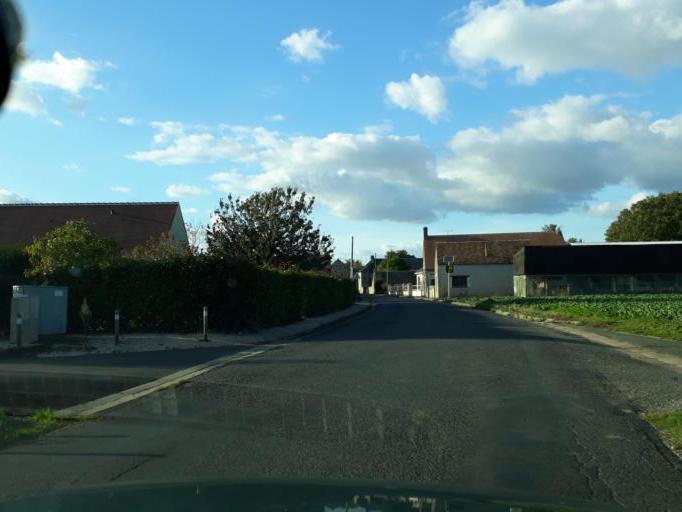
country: FR
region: Centre
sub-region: Departement du Loir-et-Cher
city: Ouzouer-le-Marche
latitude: 47.8205
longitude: 1.5018
